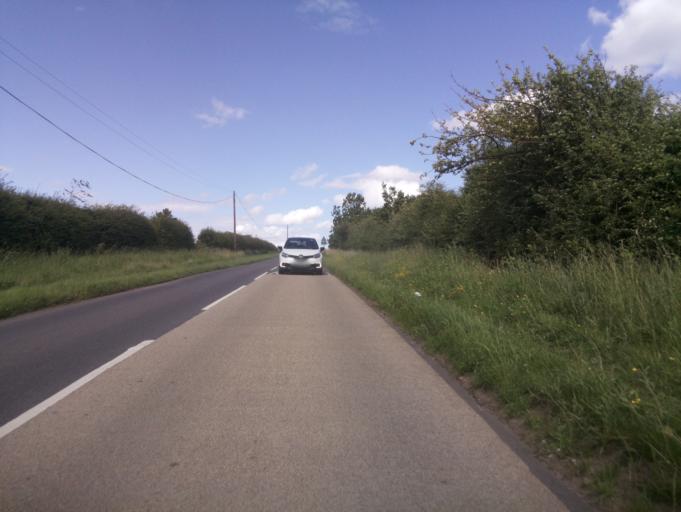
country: GB
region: England
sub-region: Nottinghamshire
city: East Leake
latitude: 52.8246
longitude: -1.1945
